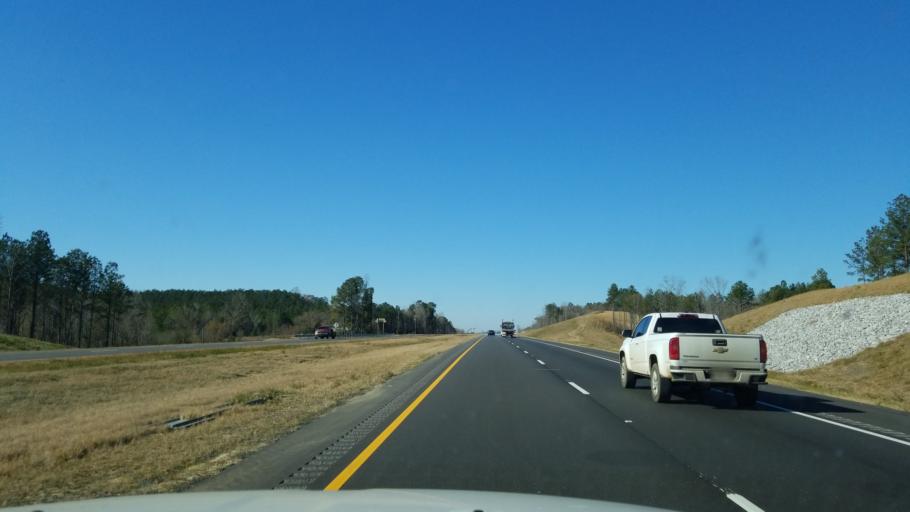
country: US
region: Alabama
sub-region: Pickens County
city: Reform
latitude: 33.3580
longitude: -87.9695
